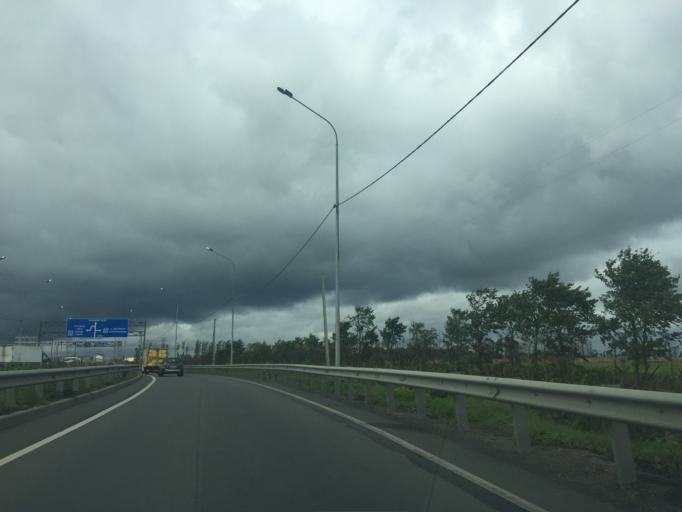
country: RU
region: St.-Petersburg
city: Aleksandrovskaya
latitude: 59.7160
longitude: 30.2938
